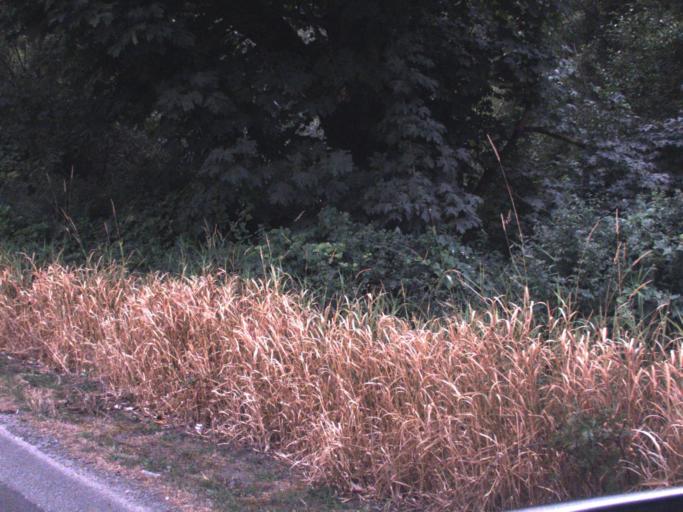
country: US
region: Washington
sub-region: King County
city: Fall City
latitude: 47.6020
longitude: -121.9134
